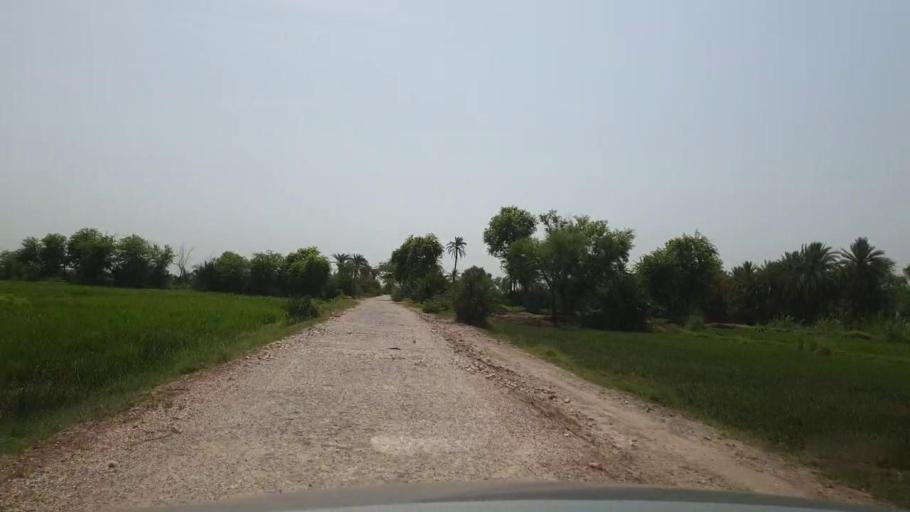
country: PK
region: Sindh
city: Garhi Yasin
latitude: 27.8964
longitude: 68.4888
